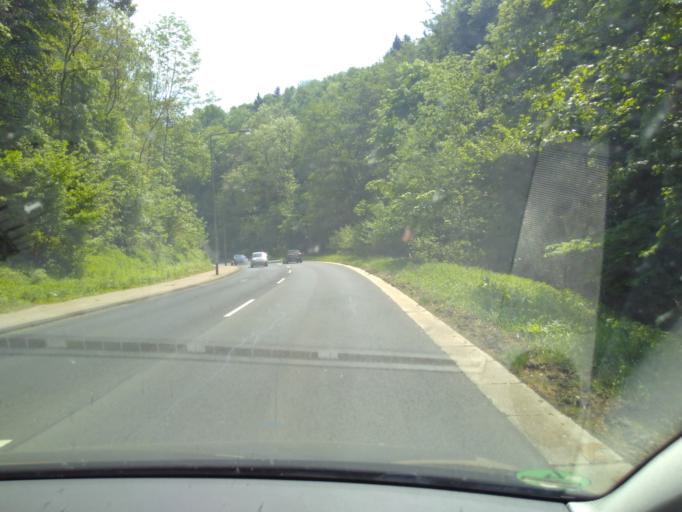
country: DE
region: Hesse
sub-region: Regierungsbezirk Kassel
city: Baunatal
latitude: 51.3048
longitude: 9.4035
